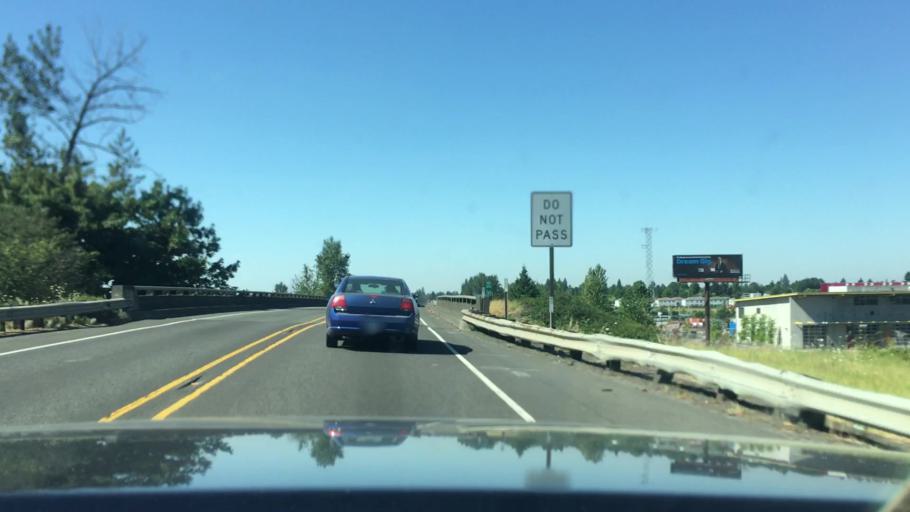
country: US
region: Oregon
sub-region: Lane County
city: Eugene
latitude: 44.0595
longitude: -123.1736
